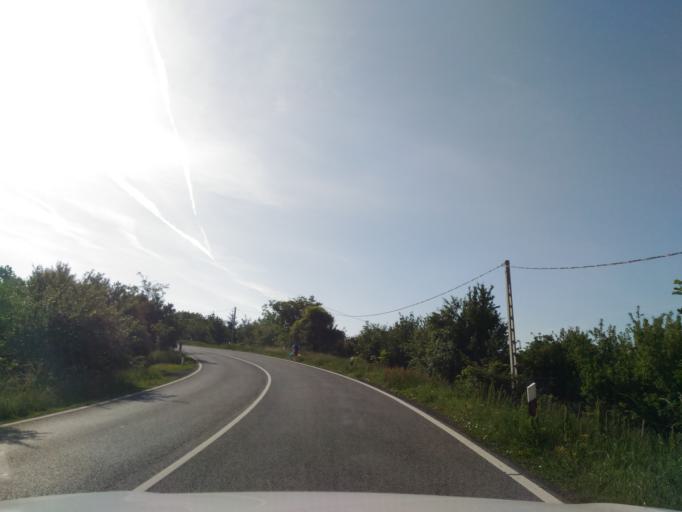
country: HU
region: Baranya
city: Komlo
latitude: 46.1761
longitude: 18.2610
